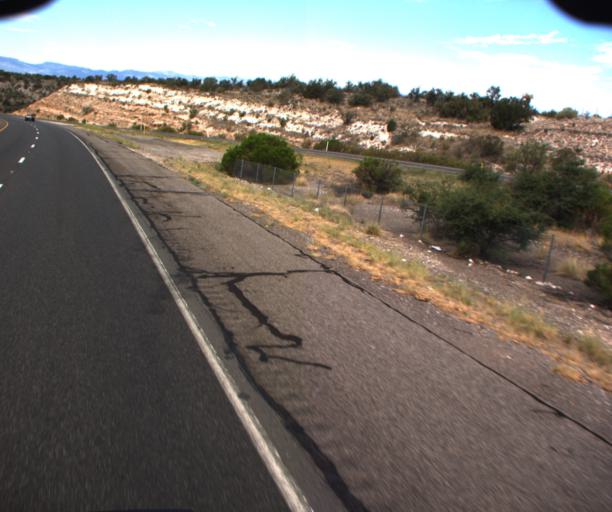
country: US
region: Arizona
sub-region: Yavapai County
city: Lake Montezuma
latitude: 34.6728
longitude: -111.7746
